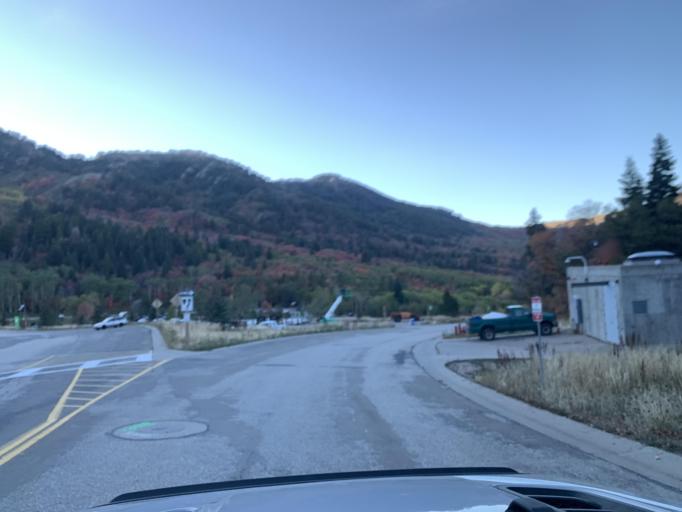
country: US
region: Utah
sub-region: Weber County
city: Uintah
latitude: 41.2171
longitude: -111.8600
